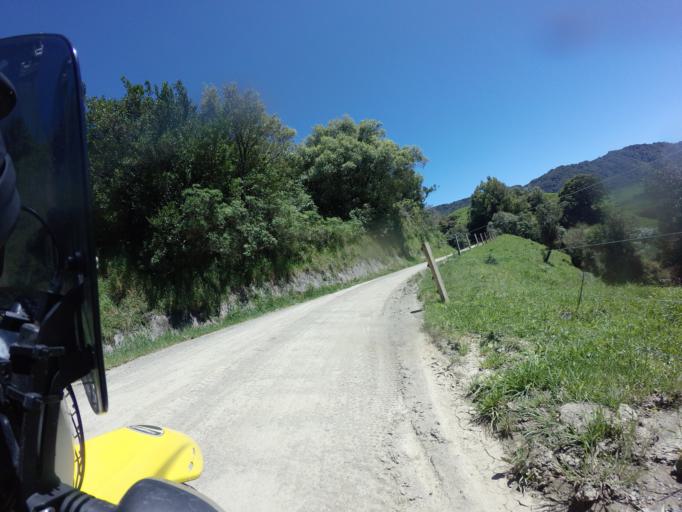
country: NZ
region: Bay of Plenty
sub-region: Opotiki District
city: Opotiki
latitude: -38.4042
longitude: 177.4544
